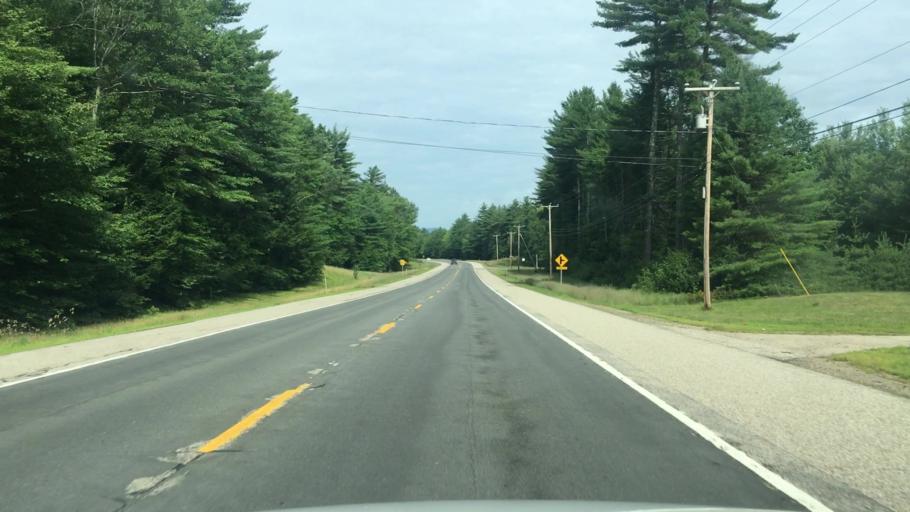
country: US
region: New Hampshire
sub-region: Carroll County
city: Tamworth
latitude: 43.8225
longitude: -71.2216
